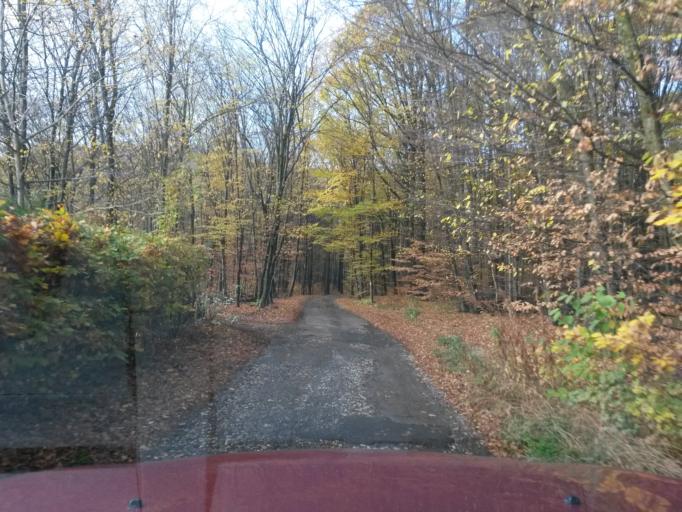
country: SK
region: Kosicky
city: Kosice
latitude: 48.7552
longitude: 21.2236
